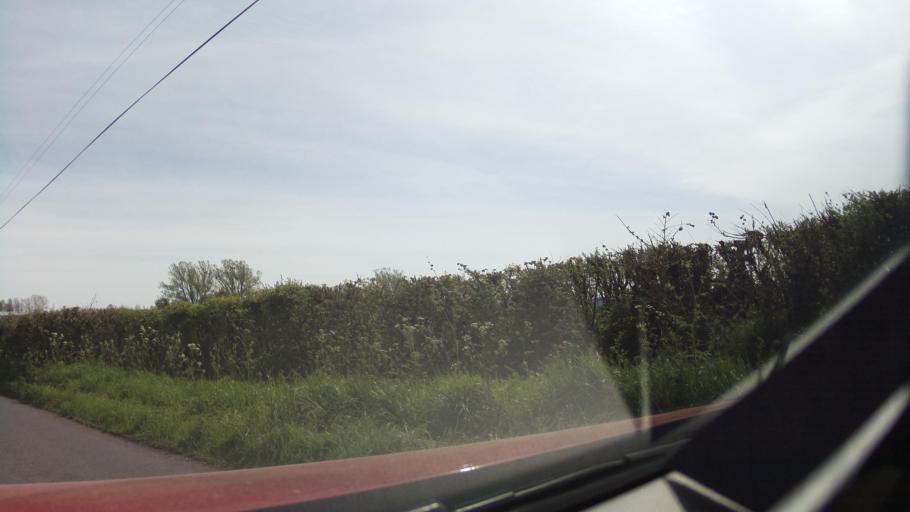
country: GB
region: England
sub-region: Somerset
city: Yeovil
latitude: 51.0174
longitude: -2.5827
